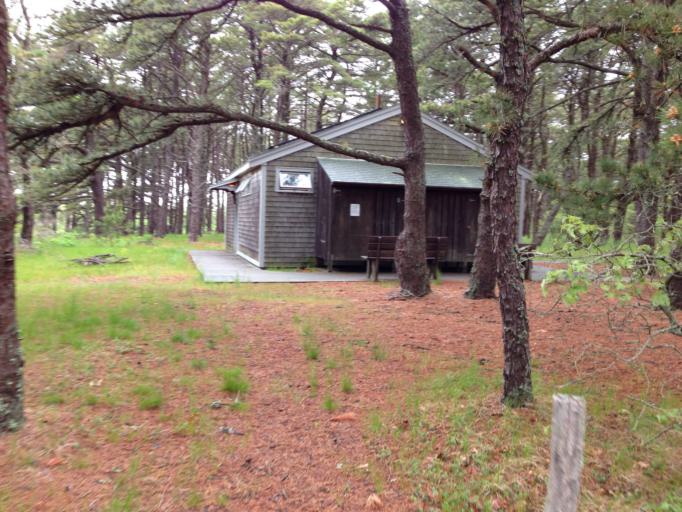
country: US
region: Massachusetts
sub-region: Barnstable County
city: North Eastham
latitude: 41.8830
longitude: -69.9928
